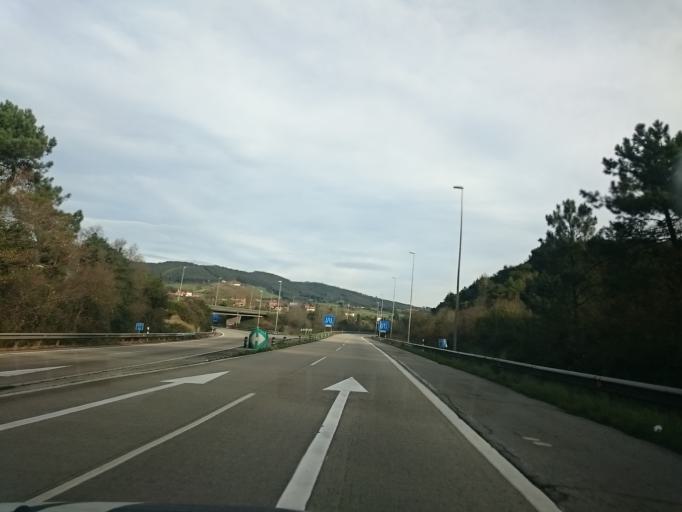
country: ES
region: Asturias
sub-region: Province of Asturias
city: Corvera de Asturias
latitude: 43.4946
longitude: -5.7866
